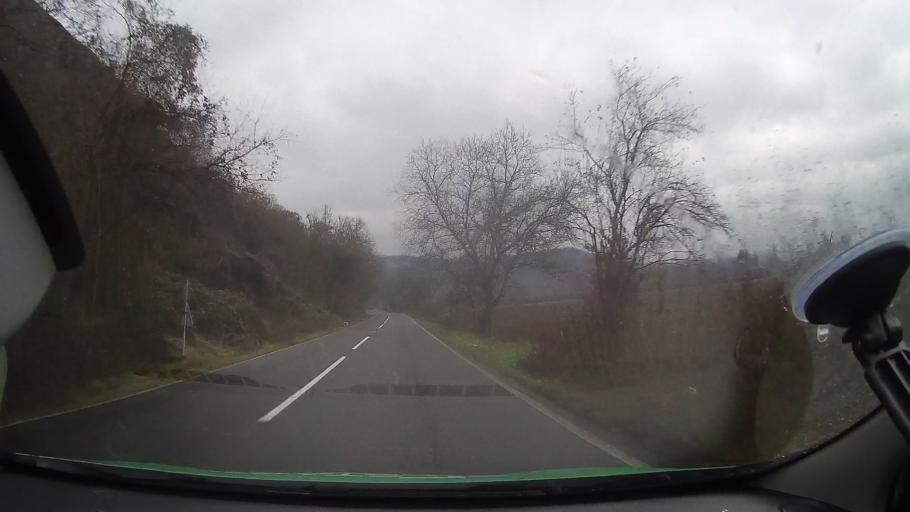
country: RO
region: Arad
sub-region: Comuna Gurahont
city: Gurahont
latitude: 46.2745
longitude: 22.3506
